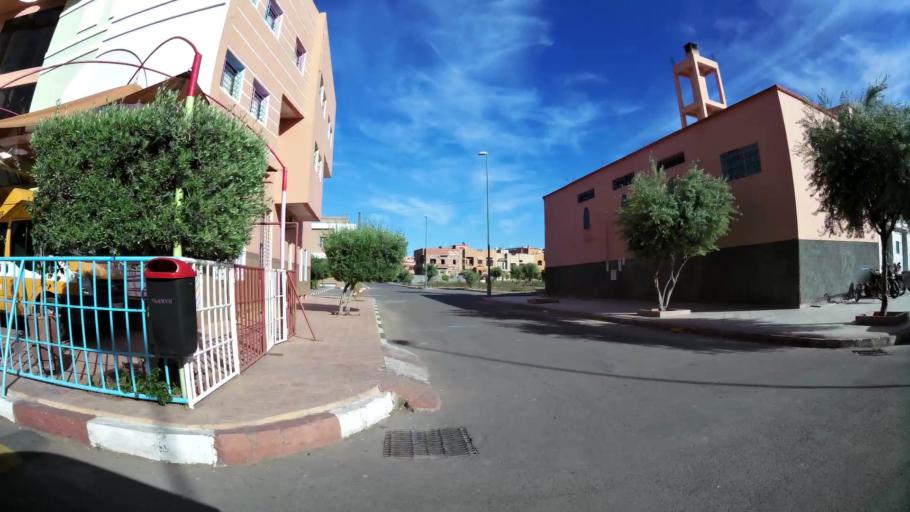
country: MA
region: Marrakech-Tensift-Al Haouz
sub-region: Marrakech
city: Marrakesh
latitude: 31.6847
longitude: -8.0657
